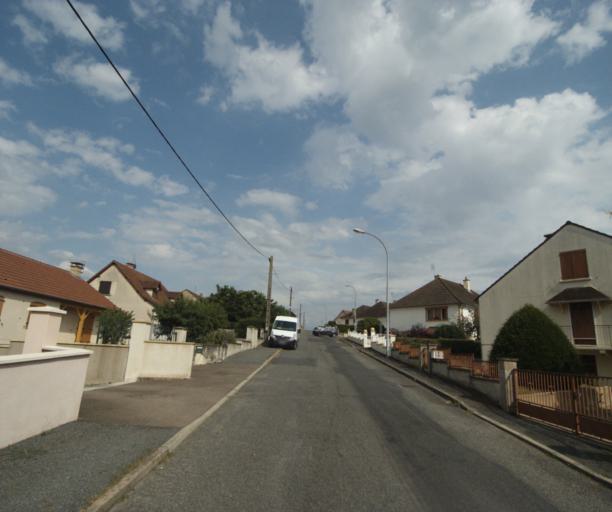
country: FR
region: Bourgogne
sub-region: Departement de Saone-et-Loire
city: Gueugnon
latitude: 46.6047
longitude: 4.0790
